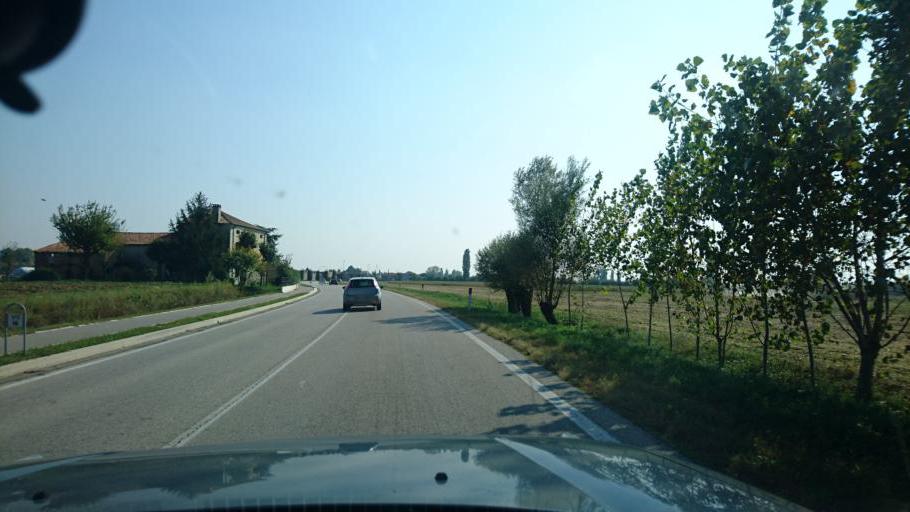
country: IT
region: Veneto
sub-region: Provincia di Padova
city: Campodoro
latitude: 45.4985
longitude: 11.7442
